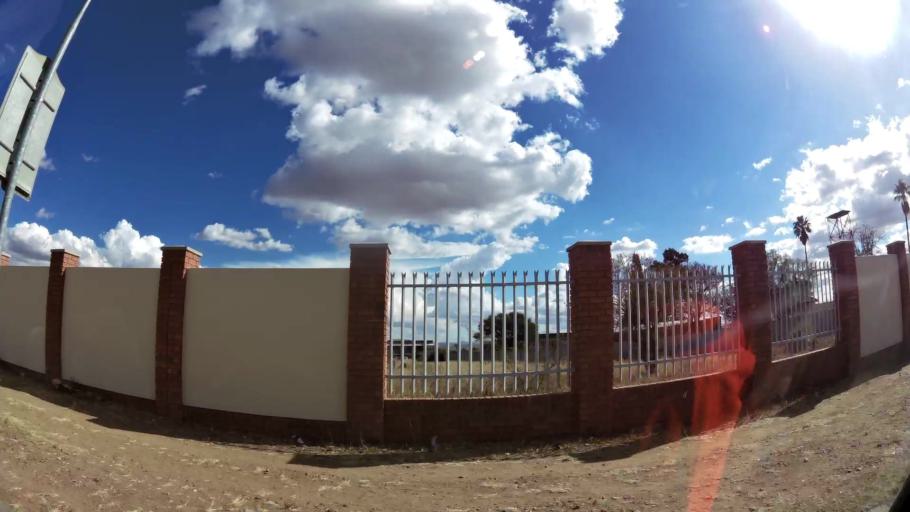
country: ZA
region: Limpopo
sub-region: Capricorn District Municipality
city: Polokwane
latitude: -23.8865
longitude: 29.4748
